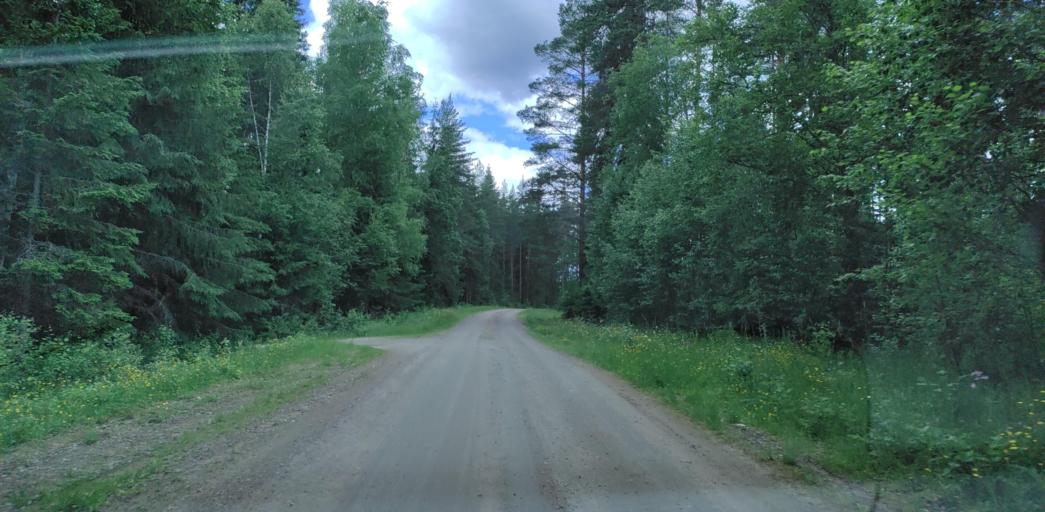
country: SE
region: Vaermland
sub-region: Hagfors Kommun
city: Ekshaerad
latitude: 60.0849
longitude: 13.4419
